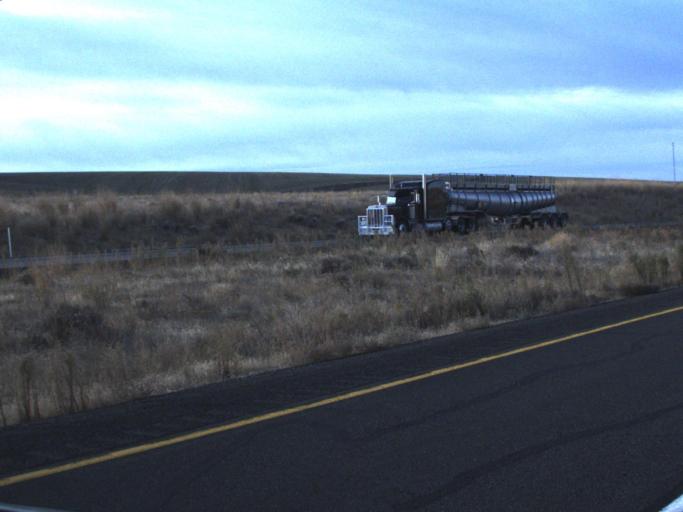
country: US
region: Washington
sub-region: Franklin County
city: Connell
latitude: 46.8373
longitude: -118.6505
